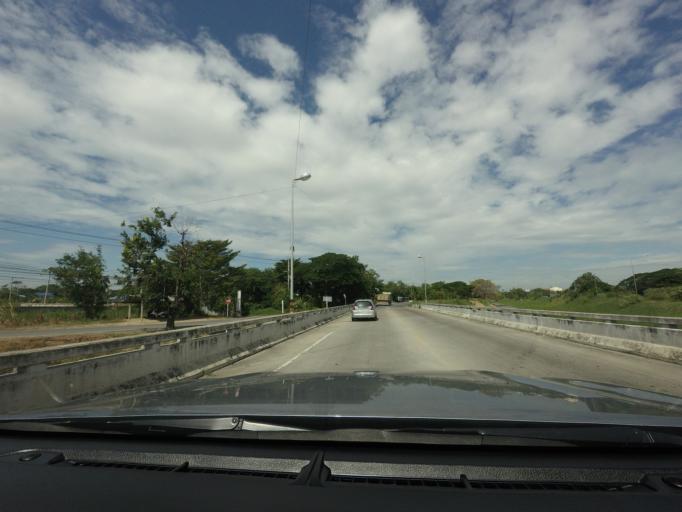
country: TH
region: Suphan Buri
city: Suphan Buri
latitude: 14.4657
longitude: 100.0912
